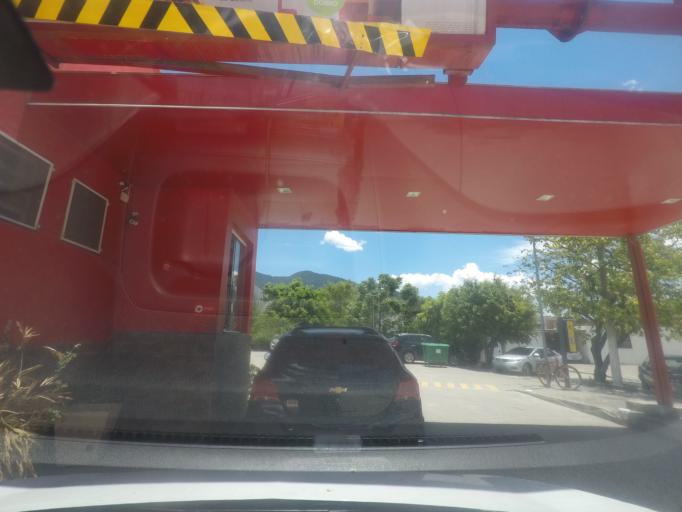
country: BR
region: Rio de Janeiro
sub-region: Nilopolis
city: Nilopolis
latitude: -22.8543
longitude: -43.4867
